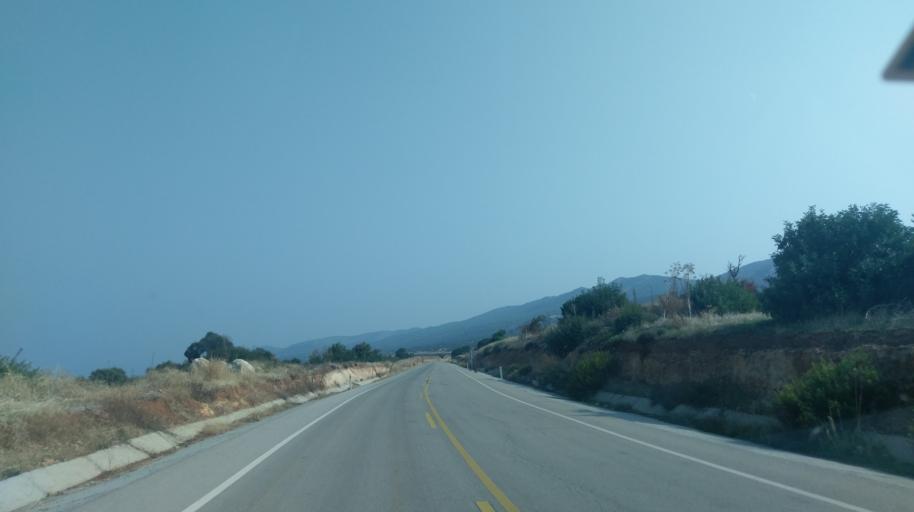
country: CY
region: Ammochostos
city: Trikomo
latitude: 35.4420
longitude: 33.9557
